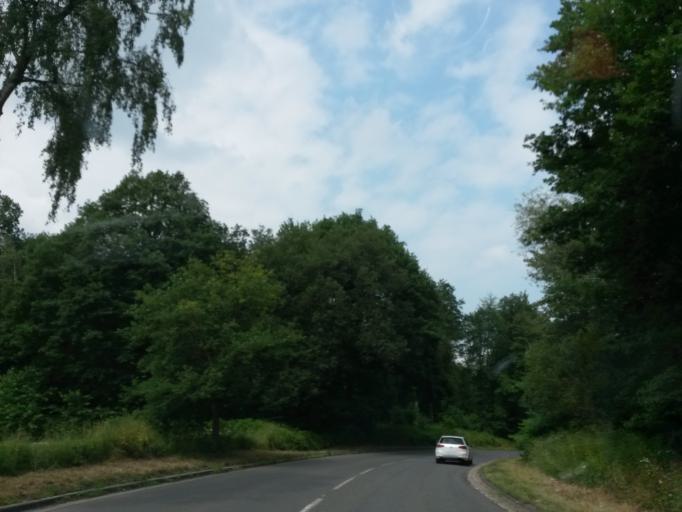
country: DE
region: North Rhine-Westphalia
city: Schwerte
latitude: 51.4020
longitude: 7.5296
